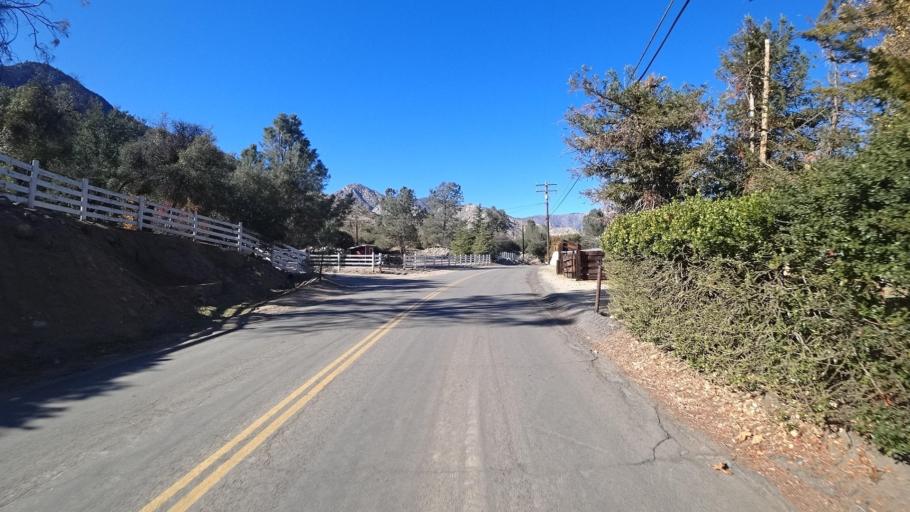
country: US
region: California
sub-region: Kern County
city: Kernville
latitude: 35.7714
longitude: -118.4393
